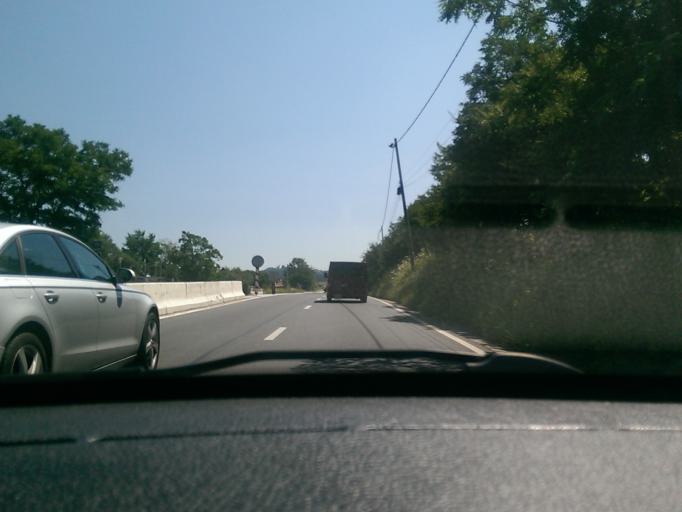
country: RO
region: Cluj
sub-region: Comuna Feleacu
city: Feleacu
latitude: 46.7317
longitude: 23.5960
